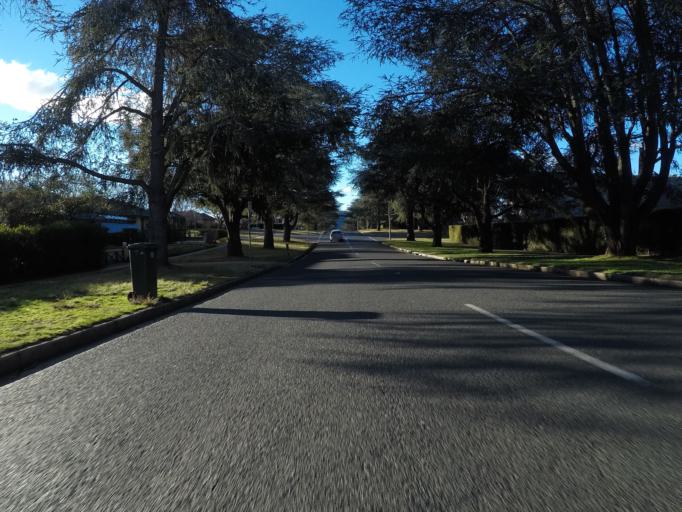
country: AU
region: Australian Capital Territory
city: Forrest
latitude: -35.3064
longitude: 149.0982
